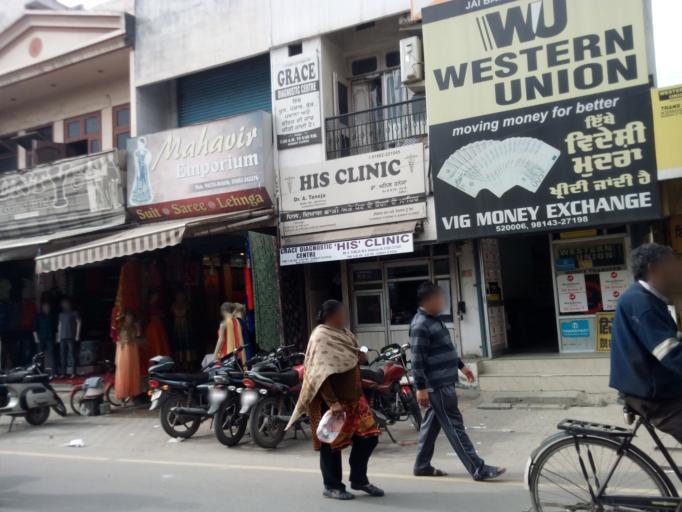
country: IN
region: Punjab
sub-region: Hoshiarpur
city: Hoshiarpur
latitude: 31.5342
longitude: 75.9082
